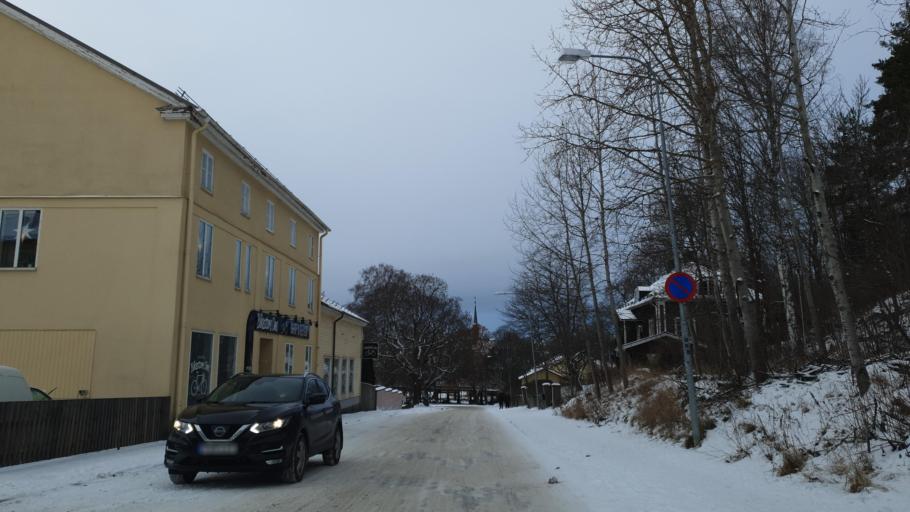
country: SE
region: Gaevleborg
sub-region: Soderhamns Kommun
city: Soderhamn
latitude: 61.2999
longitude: 17.0559
